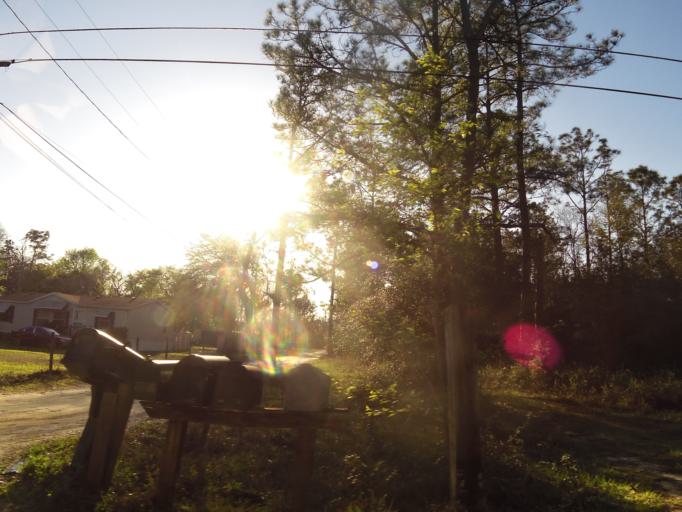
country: US
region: Florida
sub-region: Clay County
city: Middleburg
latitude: 30.1346
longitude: -81.8820
